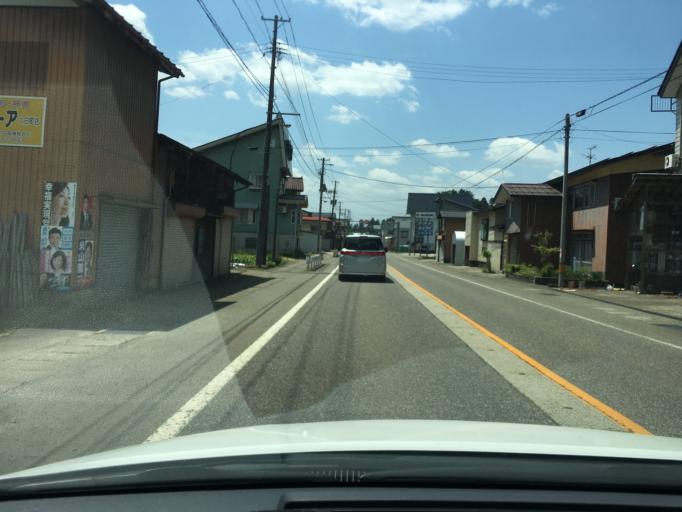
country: JP
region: Niigata
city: Tochio-honcho
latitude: 37.2971
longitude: 138.9930
